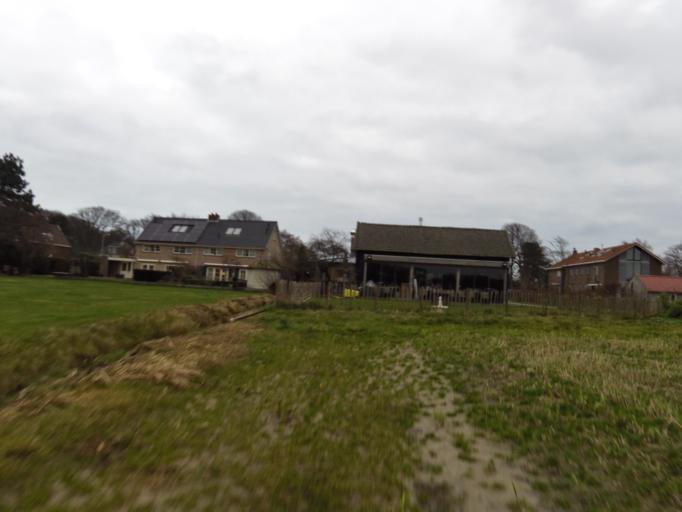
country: NL
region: North Holland
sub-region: Gemeente Bloemendaal
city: Bennebroek
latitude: 52.3312
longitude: 4.5784
